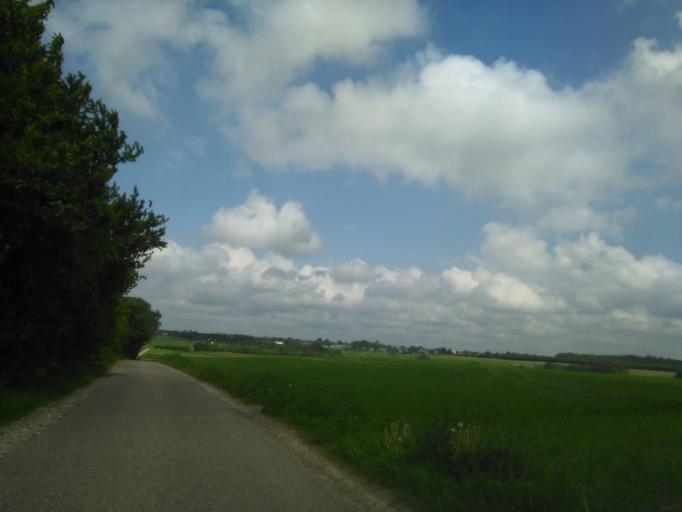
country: DK
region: Central Jutland
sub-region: Arhus Kommune
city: Sabro
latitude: 56.2094
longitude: 9.9869
